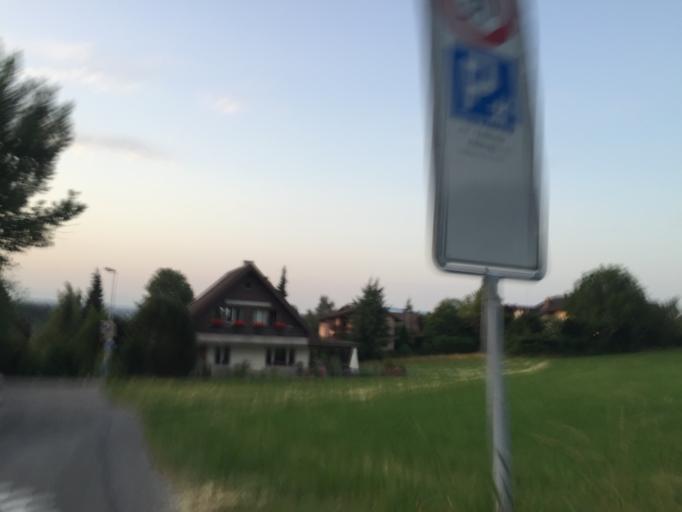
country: CH
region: Bern
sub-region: Bern-Mittelland District
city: Koniz
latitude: 46.9273
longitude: 7.4274
